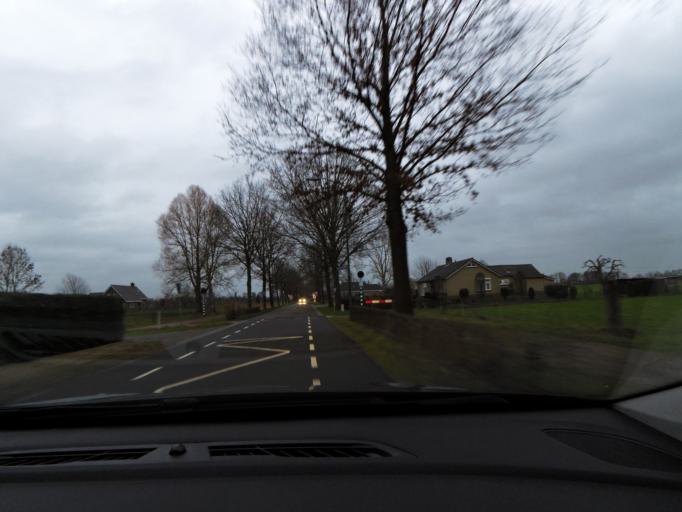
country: NL
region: North Brabant
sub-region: Gemeente Waalwijk
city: Waspik
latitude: 51.6697
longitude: 4.9835
